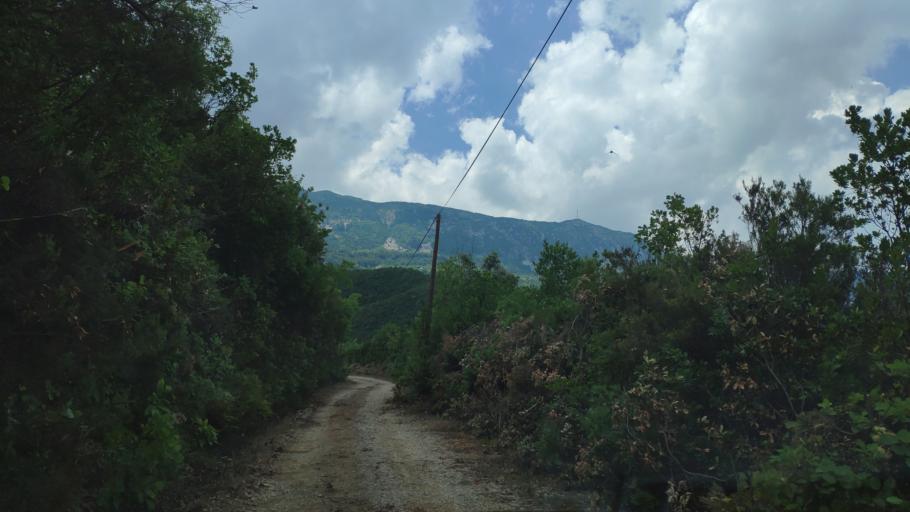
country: GR
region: Epirus
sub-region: Nomos Artas
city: Agios Dimitrios
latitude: 39.3156
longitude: 21.0170
